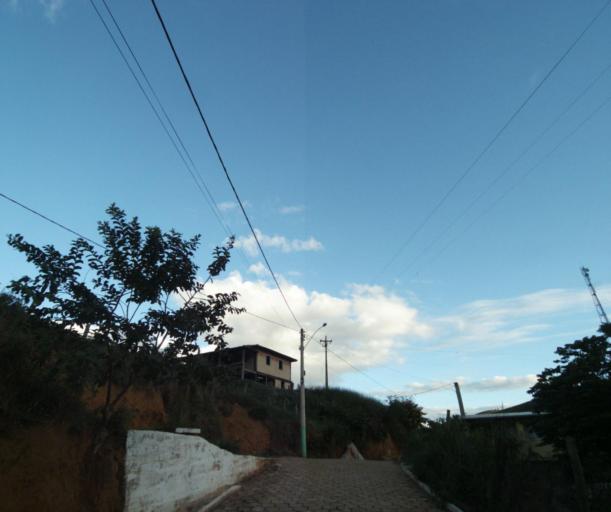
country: BR
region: Espirito Santo
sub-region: Guacui
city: Guacui
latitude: -20.6178
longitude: -41.6840
